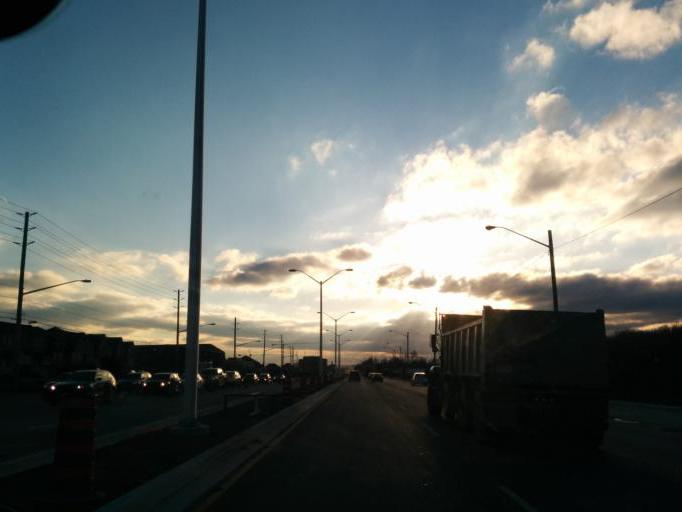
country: CA
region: Ontario
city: Oakville
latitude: 43.4432
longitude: -79.7687
